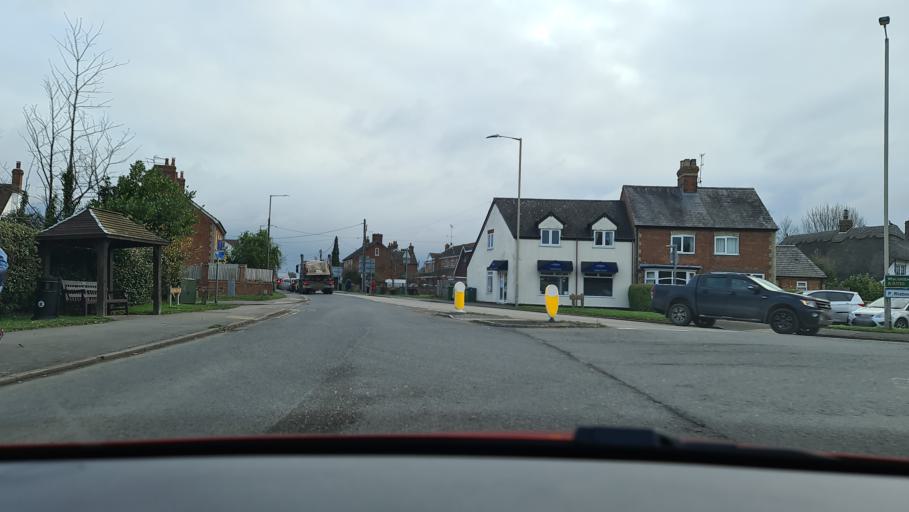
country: GB
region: England
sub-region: Buckinghamshire
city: Weston Turville
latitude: 51.7861
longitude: -0.7915
